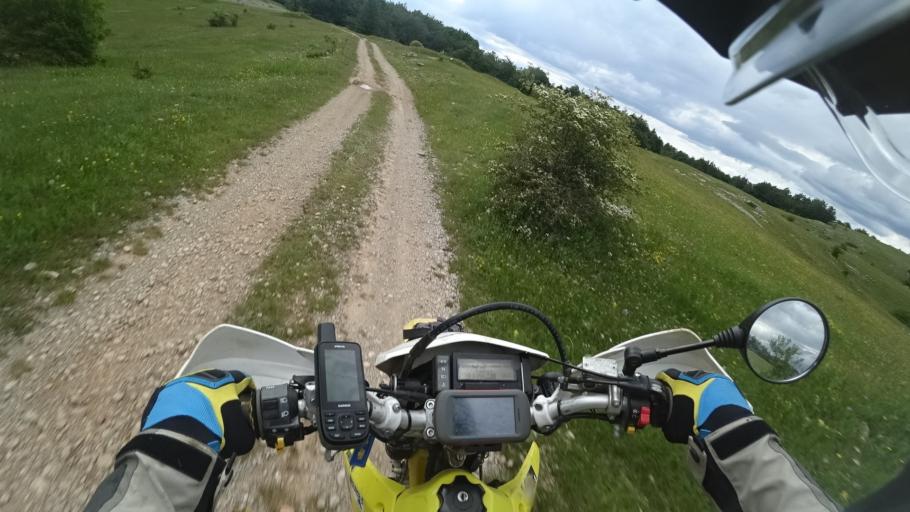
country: HR
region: Zadarska
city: Obrovac
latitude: 44.2786
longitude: 15.7214
